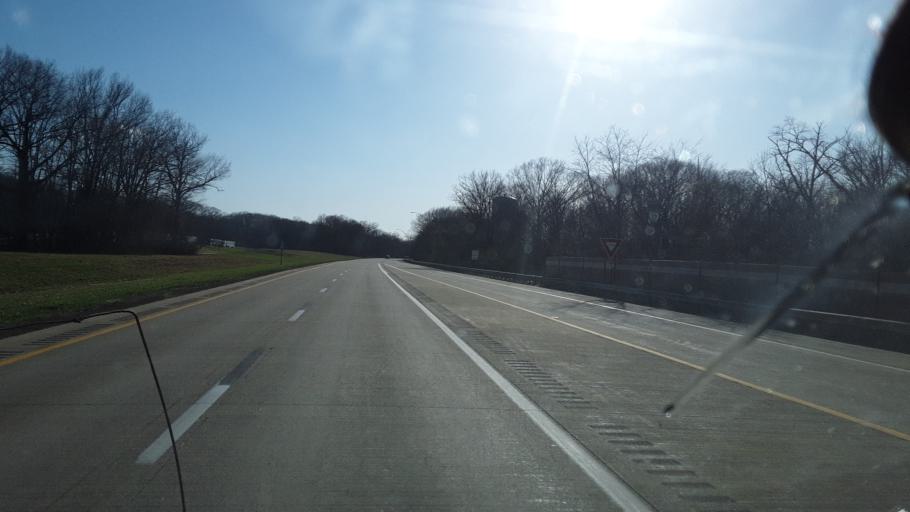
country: US
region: Ohio
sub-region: Lake County
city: Mentor
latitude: 41.6532
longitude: -81.2867
